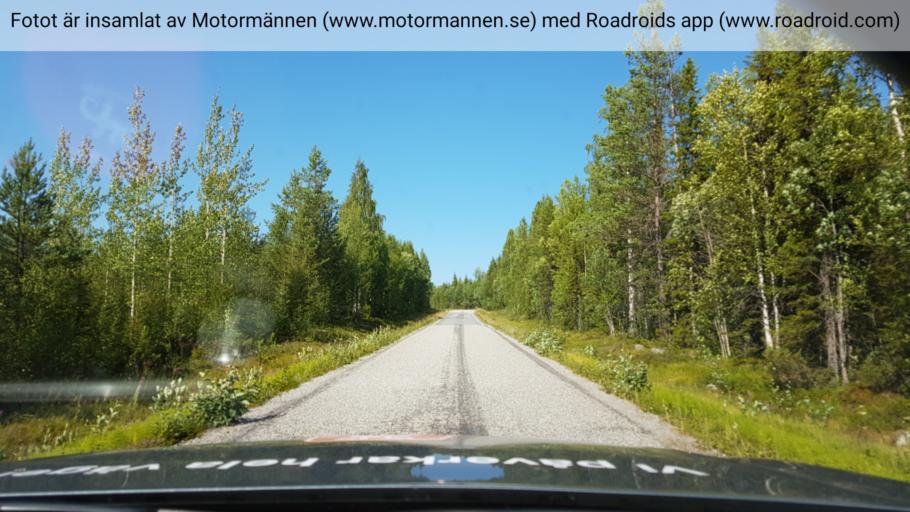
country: SE
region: Vaesterbotten
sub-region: Dorotea Kommun
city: Dorotea
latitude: 64.0446
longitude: 16.5430
